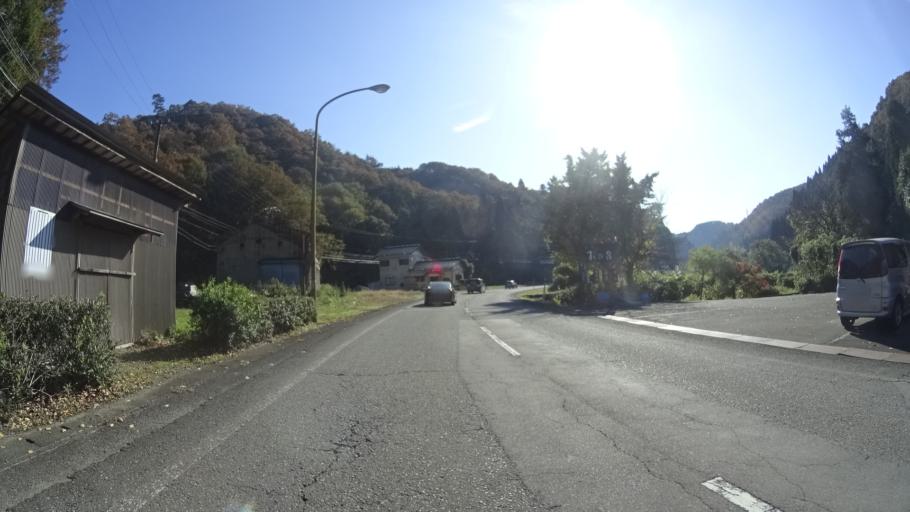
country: JP
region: Ishikawa
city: Komatsu
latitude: 36.3777
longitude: 136.5409
